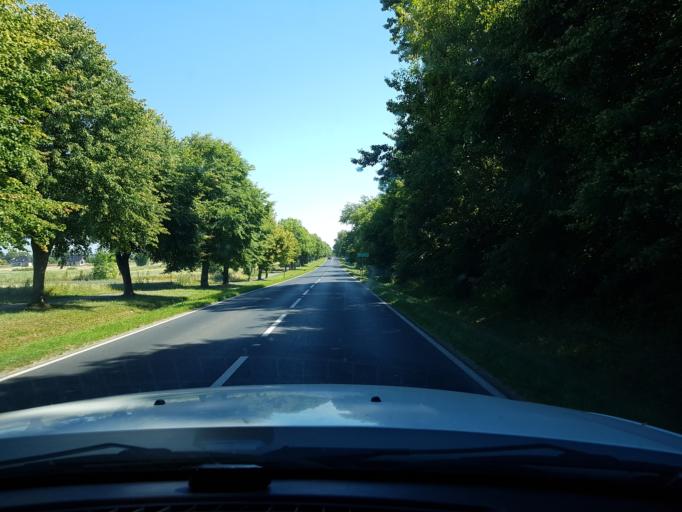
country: PL
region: West Pomeranian Voivodeship
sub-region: Powiat koszalinski
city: Mielno
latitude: 54.2456
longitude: 16.0643
